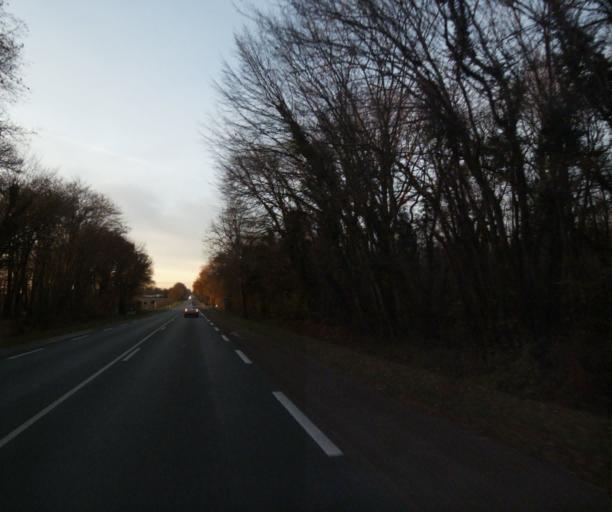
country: FR
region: Poitou-Charentes
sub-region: Departement de la Charente-Maritime
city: Saint-Georges-des-Coteaux
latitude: 45.7714
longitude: -0.6883
